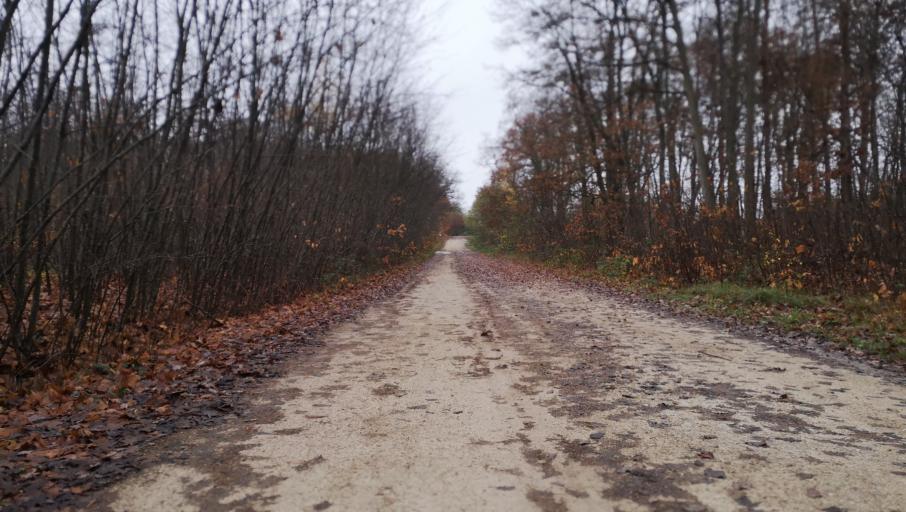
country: FR
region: Centre
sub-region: Departement du Loiret
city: Saint-Jean-de-Braye
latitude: 47.9358
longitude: 1.9822
